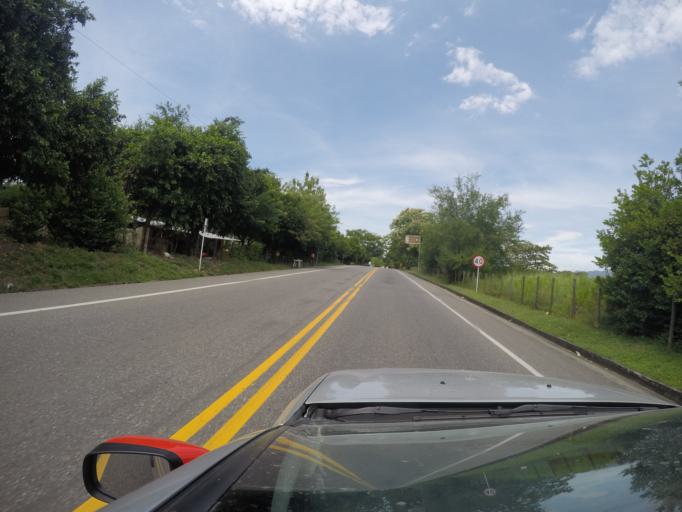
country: CO
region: Tolima
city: Honda
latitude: 5.2920
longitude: -74.7463
